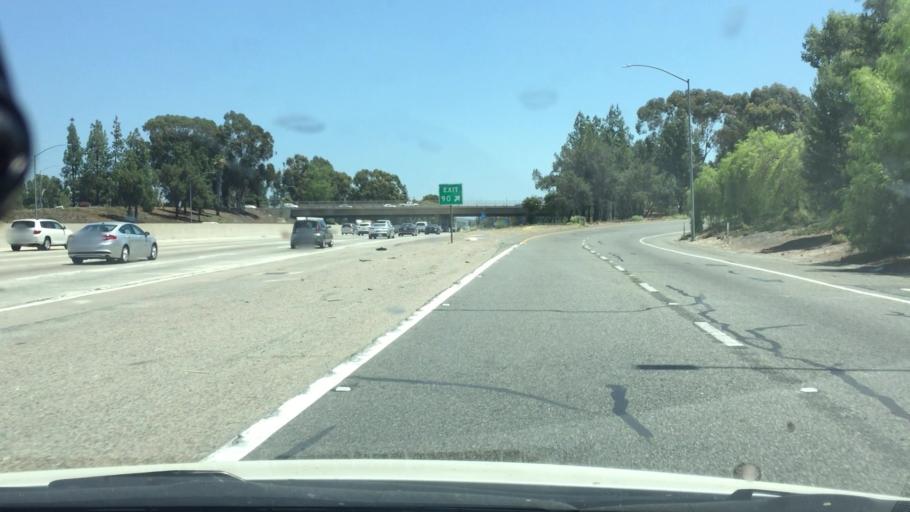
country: US
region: California
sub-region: Orange County
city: Laguna Hills
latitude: 33.6059
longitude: -117.6933
